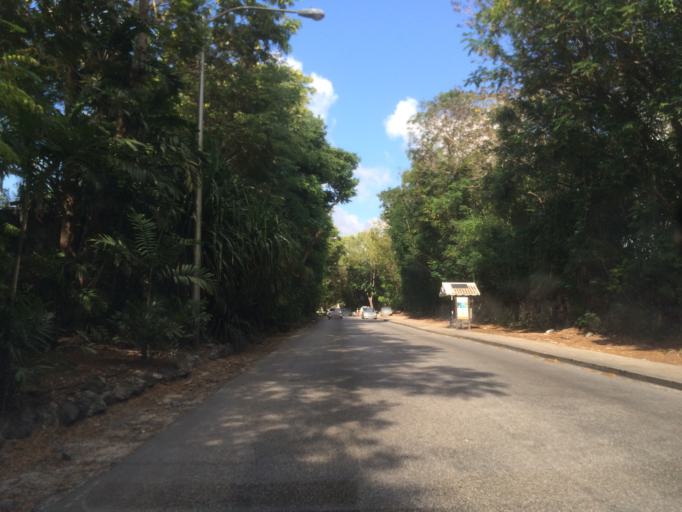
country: BB
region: Saint James
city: Holetown
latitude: 13.1710
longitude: -59.6366
